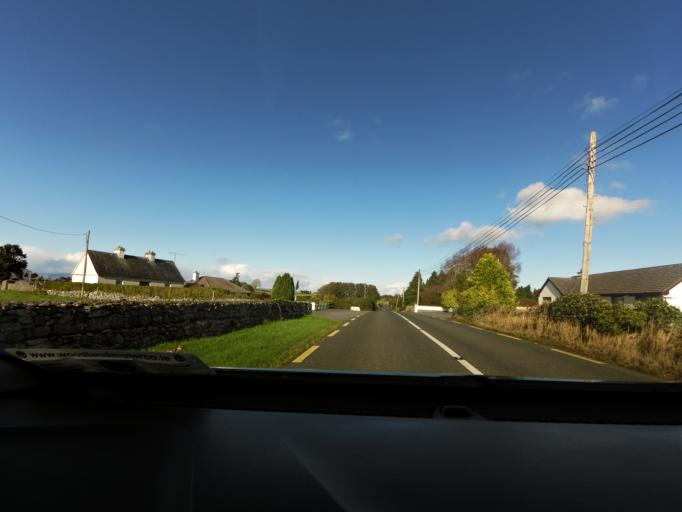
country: IE
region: Connaught
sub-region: Maigh Eo
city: Ballinrobe
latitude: 53.5609
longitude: -9.1097
